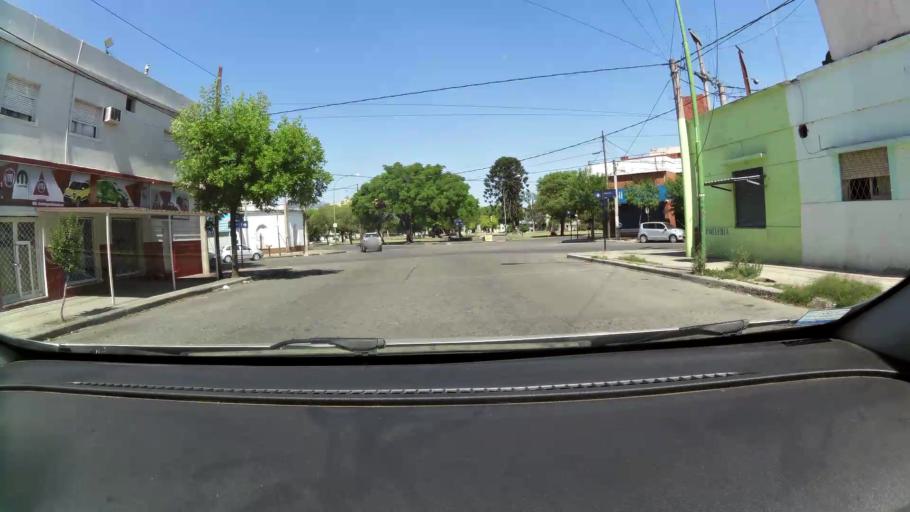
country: AR
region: Cordoba
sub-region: Departamento de Capital
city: Cordoba
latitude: -31.4008
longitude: -64.1737
